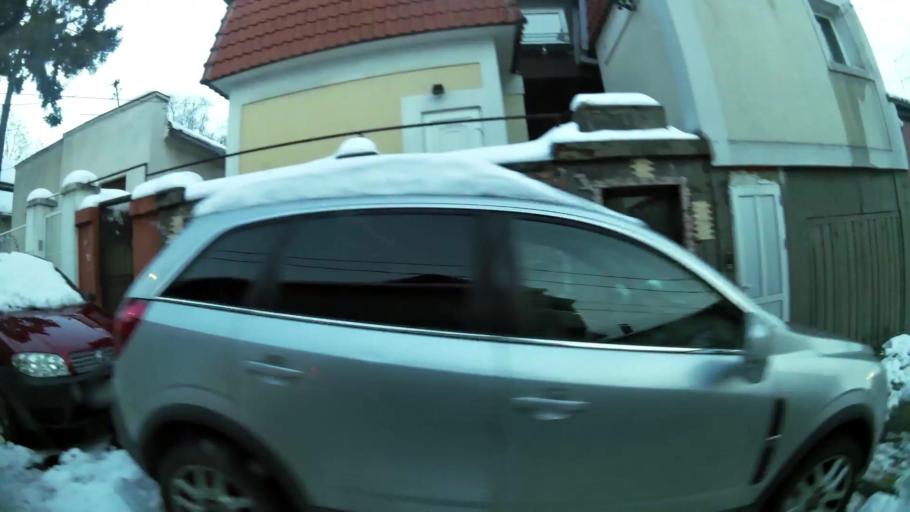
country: RS
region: Central Serbia
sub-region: Belgrade
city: Palilula
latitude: 44.8016
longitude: 20.4980
